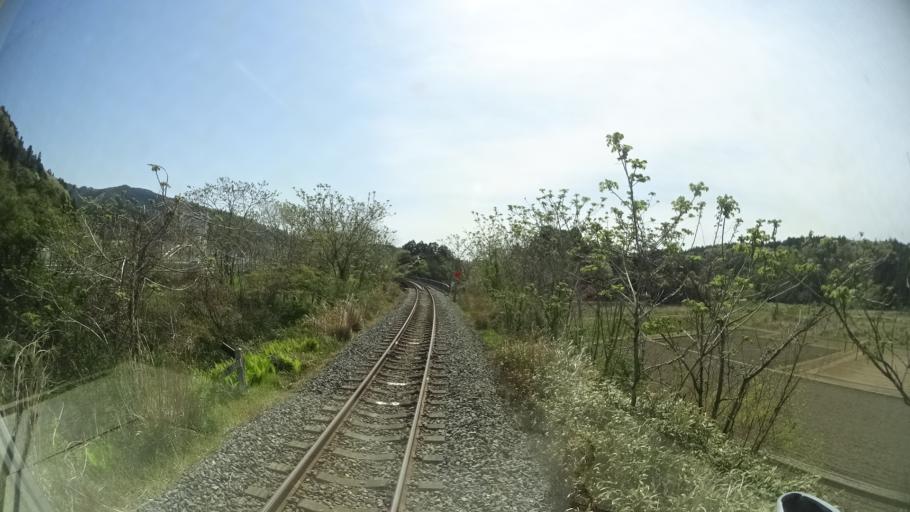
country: JP
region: Iwate
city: Ofunato
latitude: 38.9123
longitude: 141.5386
